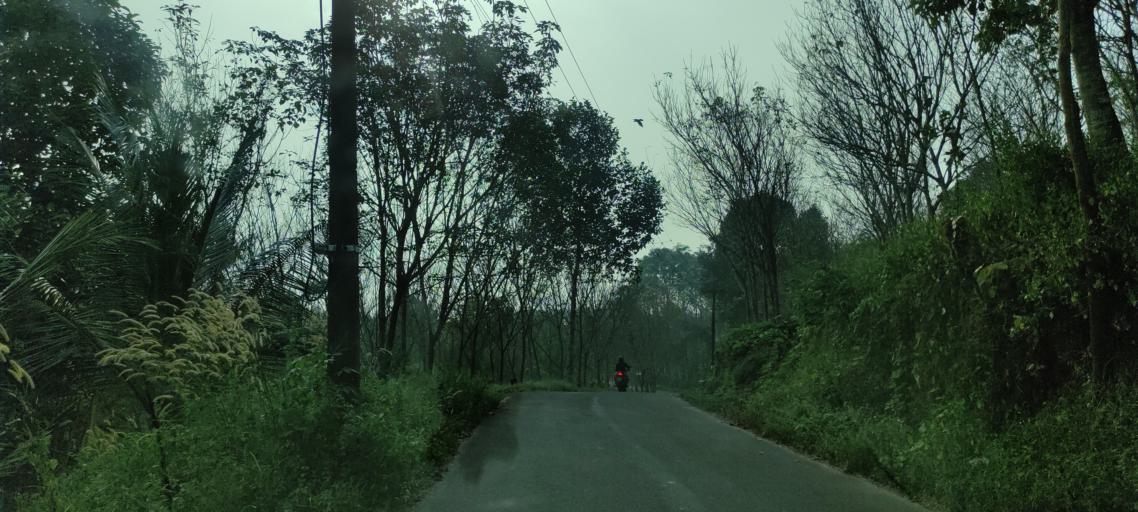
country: IN
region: Kerala
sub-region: Ernakulam
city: Piravam
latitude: 9.8006
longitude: 76.5033
